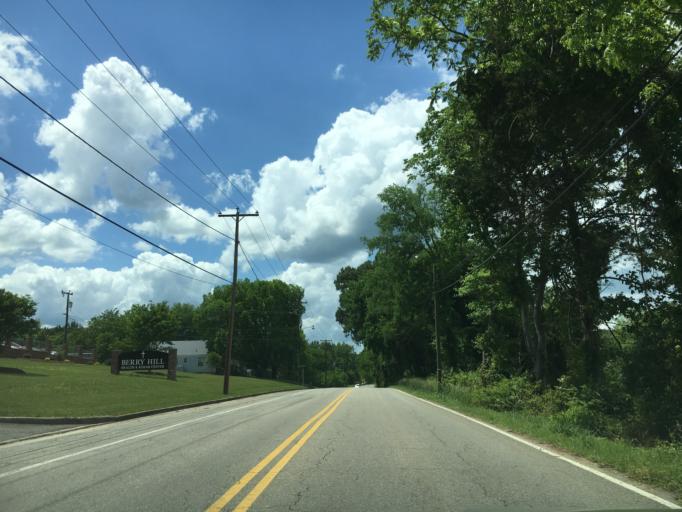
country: US
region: Virginia
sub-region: Halifax County
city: South Boston
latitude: 36.6986
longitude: -78.9194
